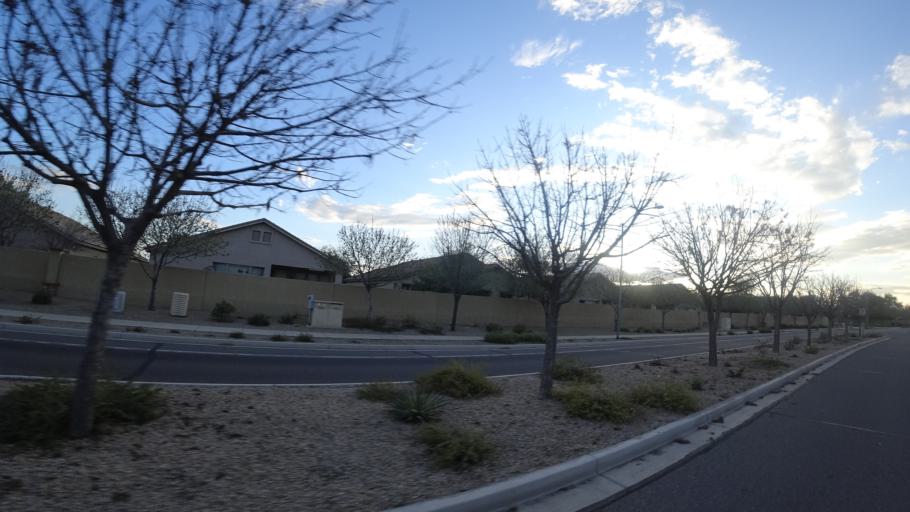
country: US
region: Arizona
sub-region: Maricopa County
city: Peoria
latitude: 33.5418
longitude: -112.2398
